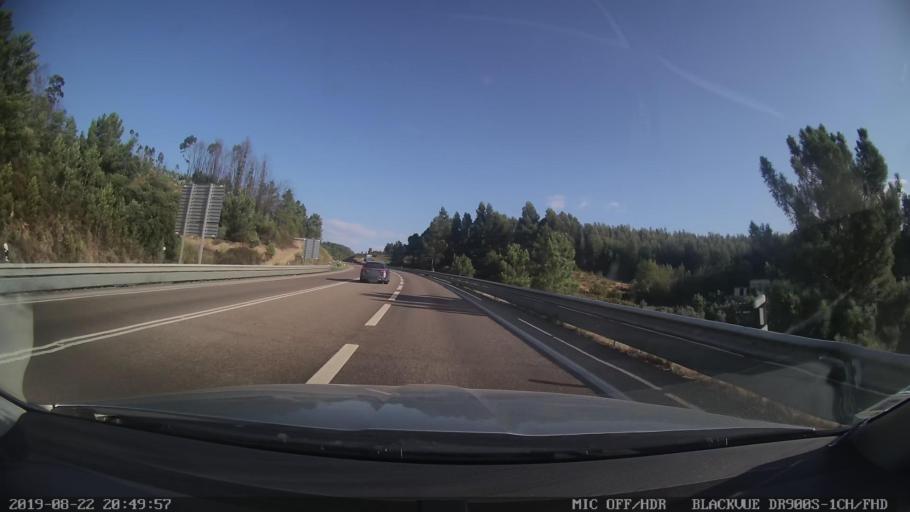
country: PT
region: Castelo Branco
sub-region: Proenca-A-Nova
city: Proenca-a-Nova
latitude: 39.7491
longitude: -7.9344
